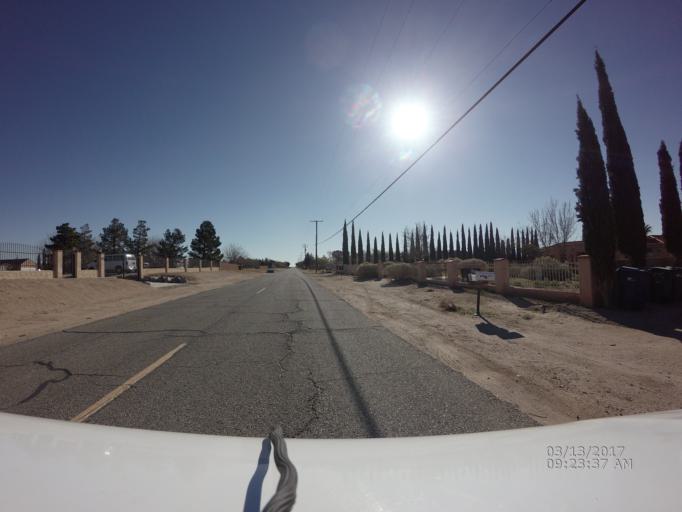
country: US
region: California
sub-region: Los Angeles County
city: Quartz Hill
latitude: 34.7619
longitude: -118.2795
